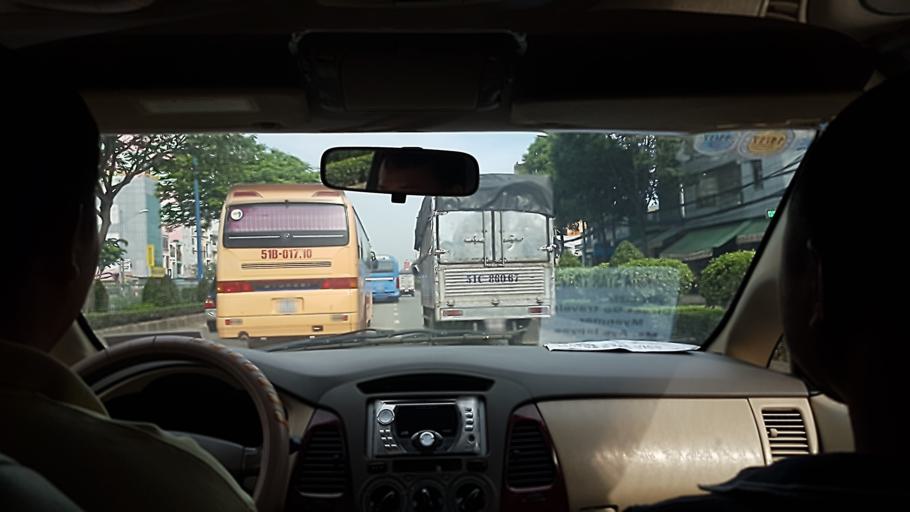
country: VN
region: Ho Chi Minh City
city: Ho Chi Minh City
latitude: 10.8324
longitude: 106.6219
